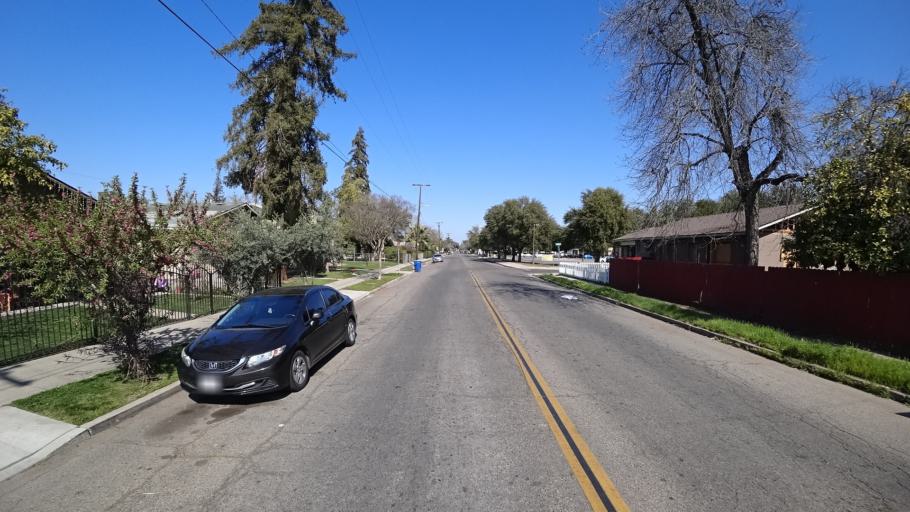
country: US
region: California
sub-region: Fresno County
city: Fresno
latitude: 36.7519
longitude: -119.7951
